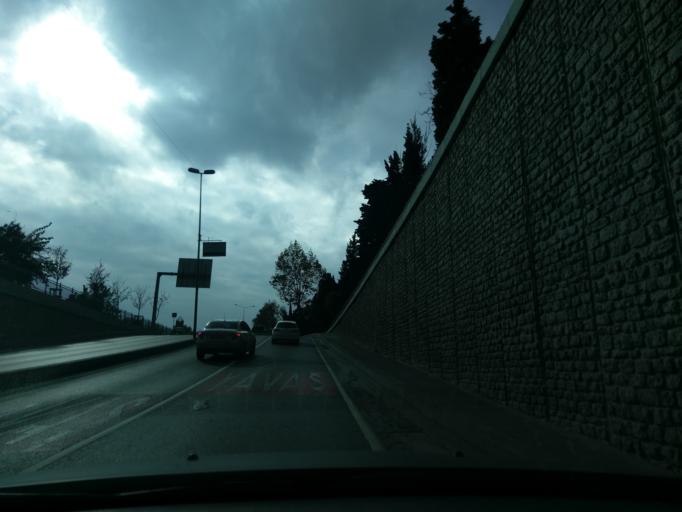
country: TR
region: Istanbul
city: Istanbul
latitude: 41.0162
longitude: 28.9218
